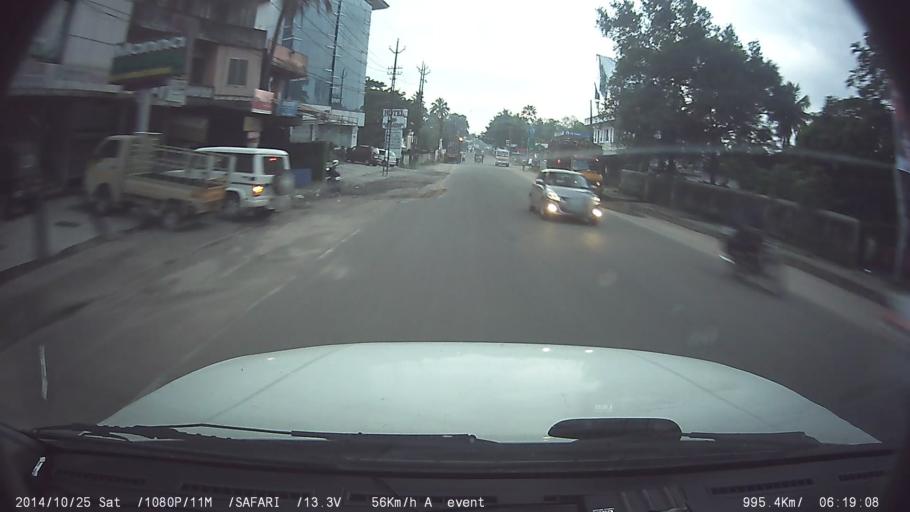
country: IN
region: Kerala
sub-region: Ernakulam
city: Perumpavur
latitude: 10.1100
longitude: 76.4801
